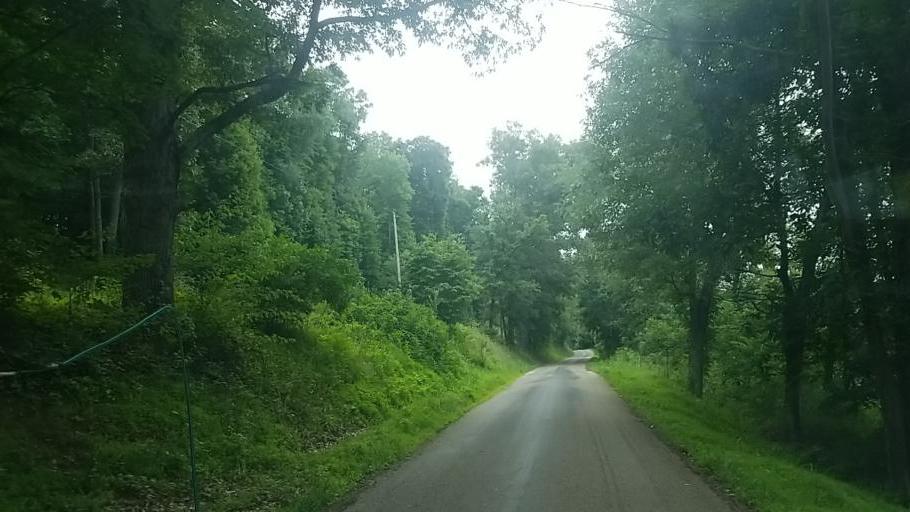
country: US
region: Ohio
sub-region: Muskingum County
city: Frazeysburg
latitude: 40.2379
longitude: -82.2146
